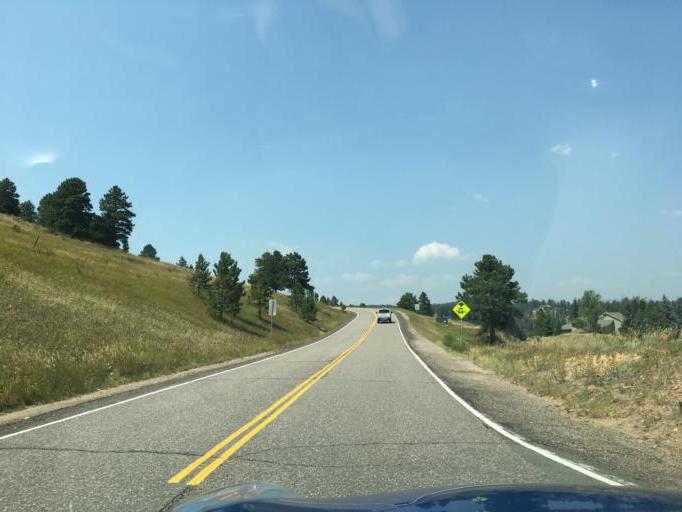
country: US
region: Colorado
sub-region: Jefferson County
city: Genesee
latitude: 39.7030
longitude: -105.2748
